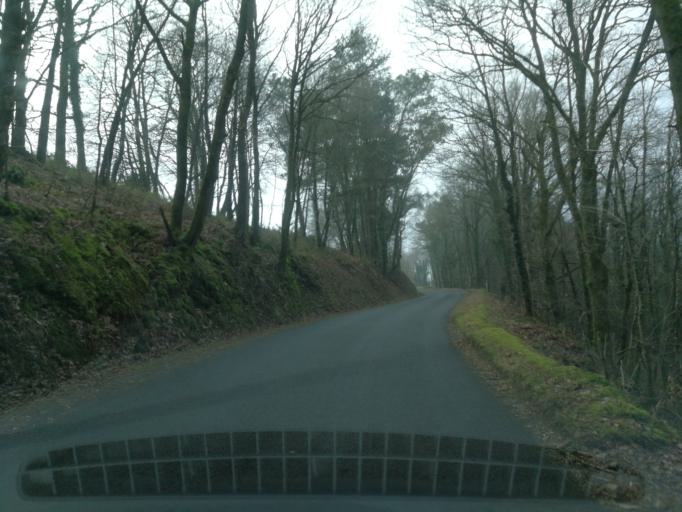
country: FR
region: Brittany
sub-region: Departement du Morbihan
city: La Vraie-Croix
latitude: 47.7302
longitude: -2.5070
